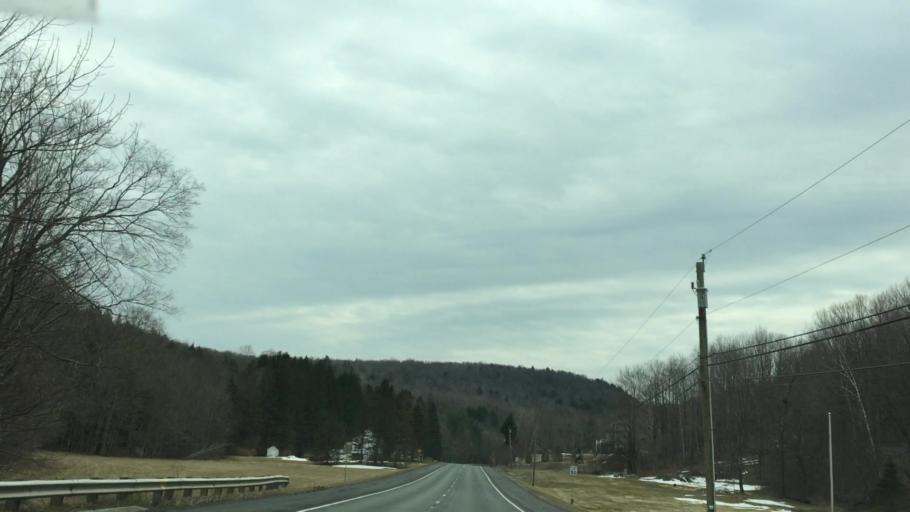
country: US
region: Massachusetts
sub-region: Berkshire County
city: Williamstown
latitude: 42.6223
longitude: -73.2308
